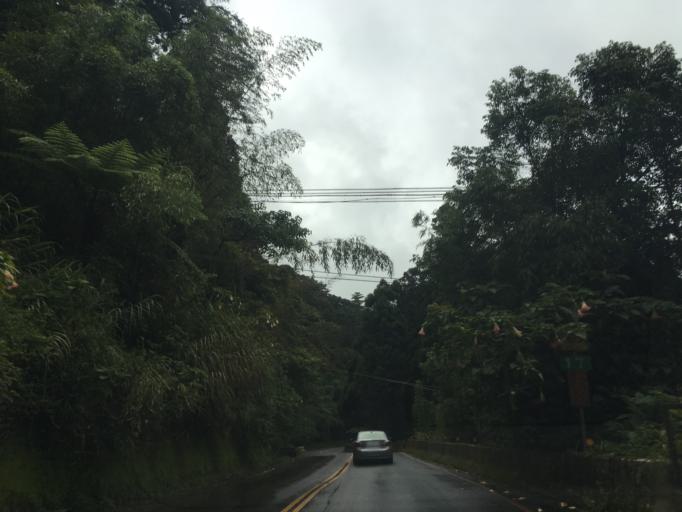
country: TW
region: Taiwan
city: Lugu
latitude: 23.5045
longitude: 120.6979
